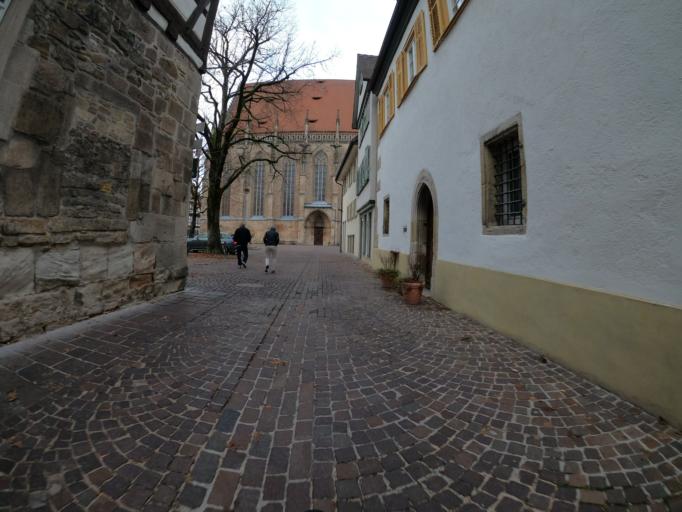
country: DE
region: Baden-Wuerttemberg
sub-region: Regierungsbezirk Stuttgart
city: Schwabisch Gmund
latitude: 48.7984
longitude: 9.7967
